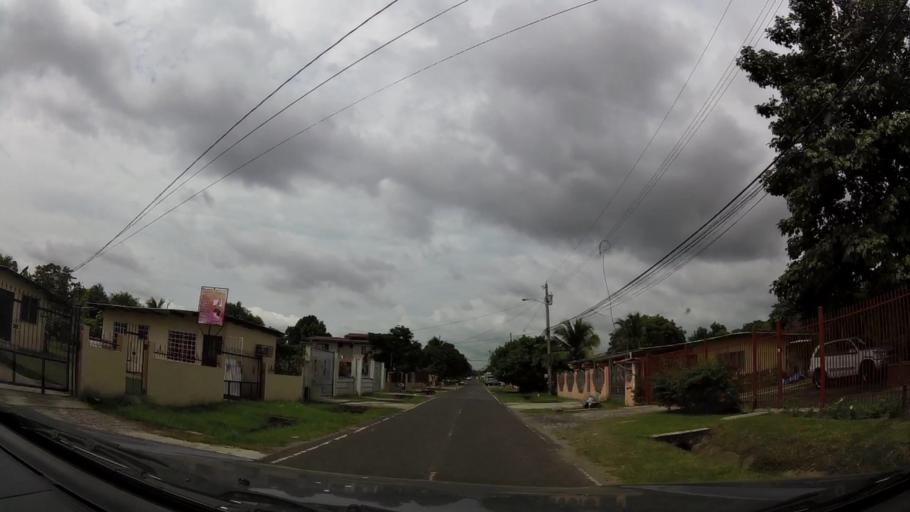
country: PA
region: Panama
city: San Miguelito
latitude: 9.0467
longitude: -79.4232
